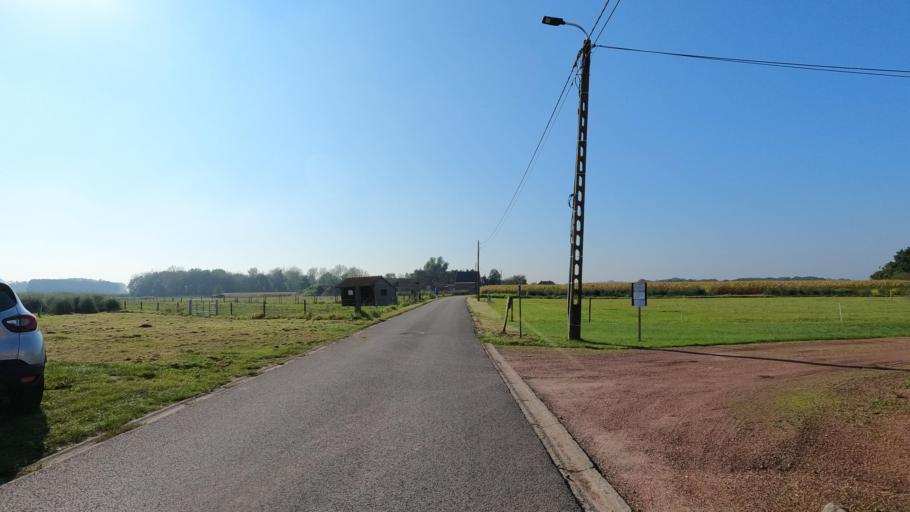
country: BE
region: Flanders
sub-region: Provincie Vlaams-Brabant
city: Tremelo
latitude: 50.9886
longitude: 4.6722
